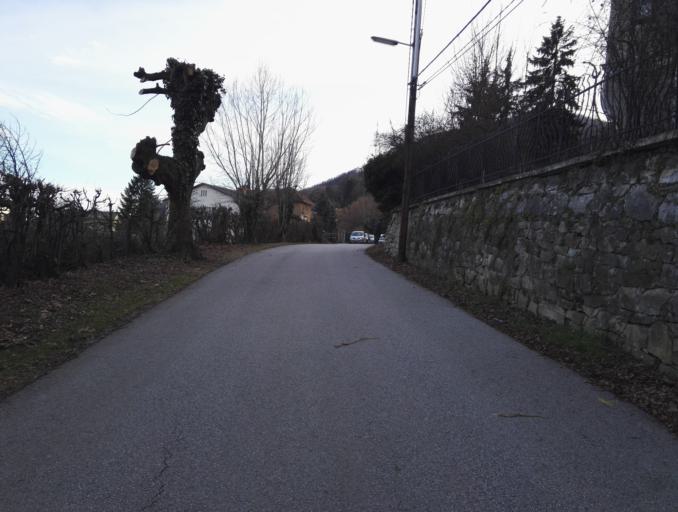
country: AT
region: Styria
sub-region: Graz Stadt
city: Goesting
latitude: 47.1044
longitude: 15.3937
